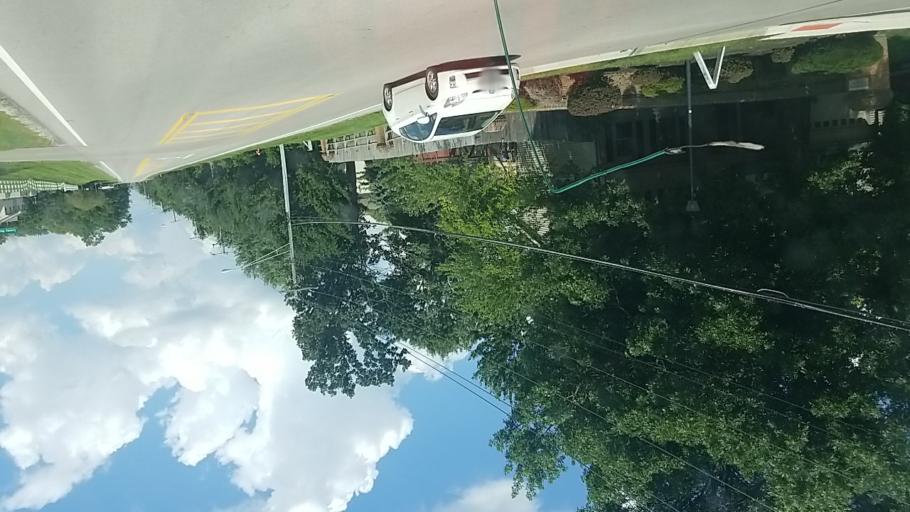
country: US
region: Ohio
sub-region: Franklin County
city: Worthington
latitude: 40.1271
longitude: -83.0002
